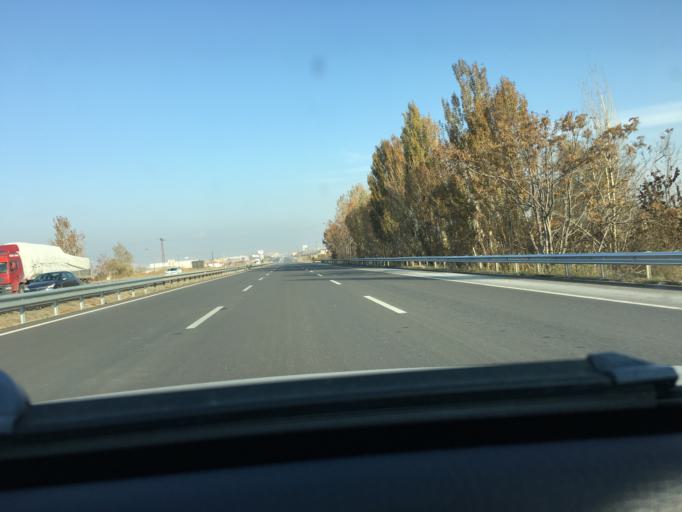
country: TR
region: Ankara
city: Temelli
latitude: 39.7166
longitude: 32.3116
